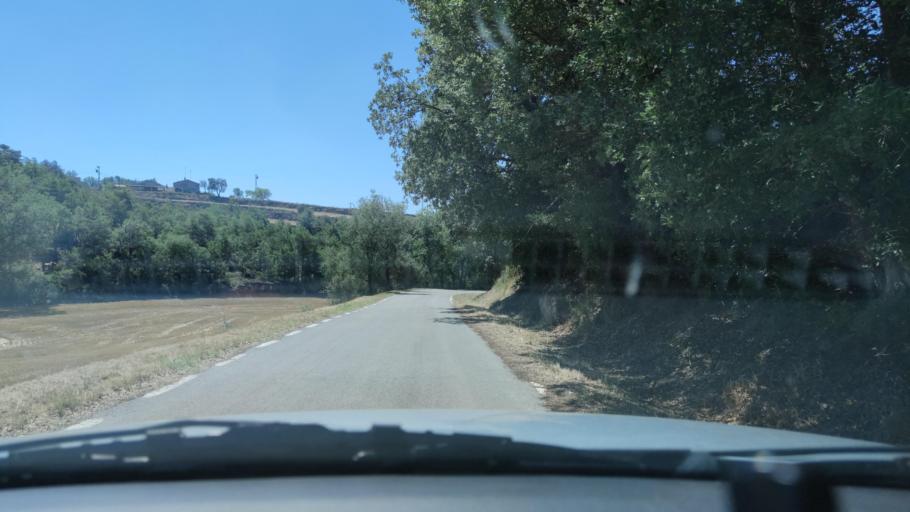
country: ES
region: Catalonia
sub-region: Provincia de Lleida
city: Tora de Riubregos
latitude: 41.8513
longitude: 1.4266
